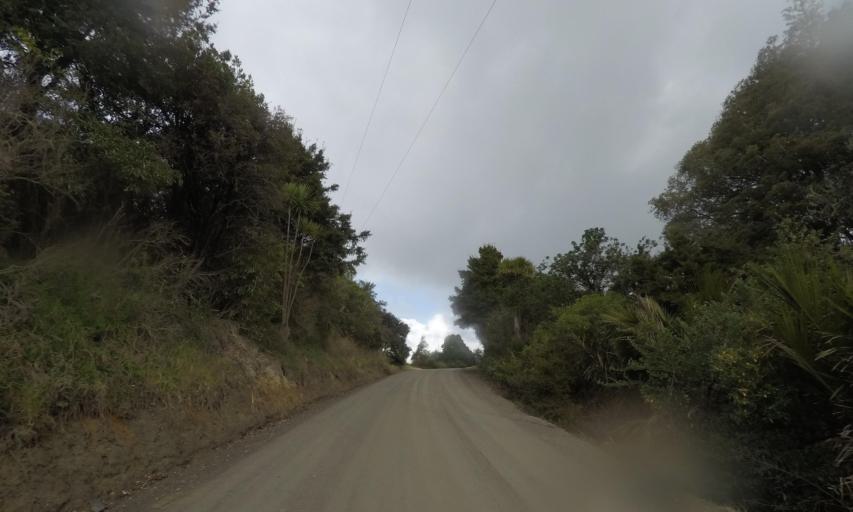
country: NZ
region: Auckland
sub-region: Auckland
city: Wellsford
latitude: -36.1704
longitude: 174.6017
